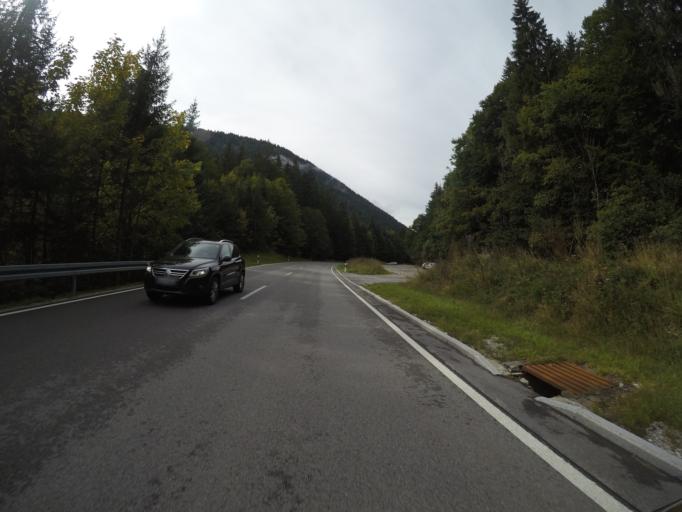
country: DE
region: Bavaria
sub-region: Upper Bavaria
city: Lenggries
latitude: 47.5837
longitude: 11.5977
